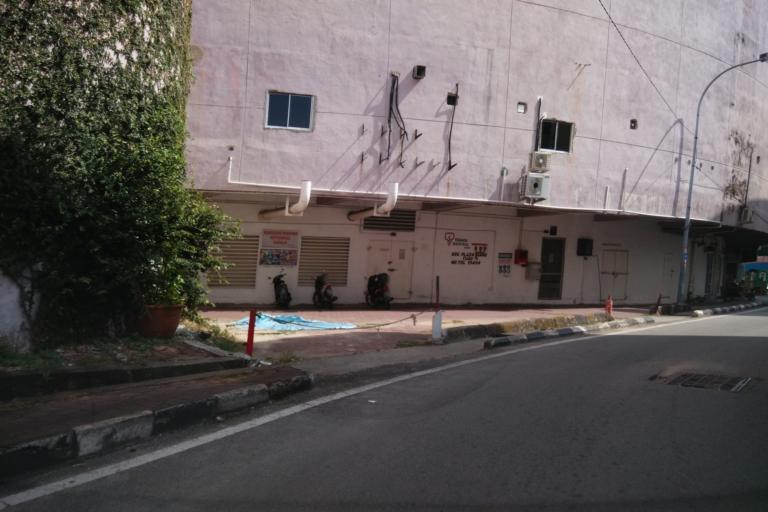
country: MY
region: Melaka
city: Malacca
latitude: 2.2022
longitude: 102.2482
